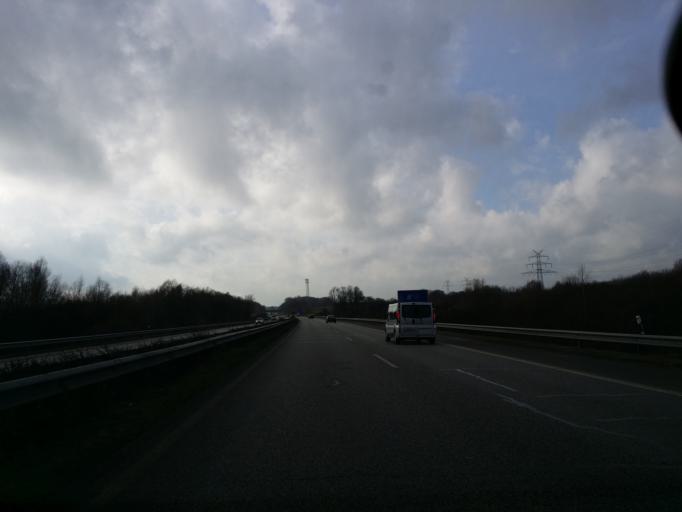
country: DE
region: Schleswig-Holstein
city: Achterwehr
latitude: 54.3200
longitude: 9.9649
